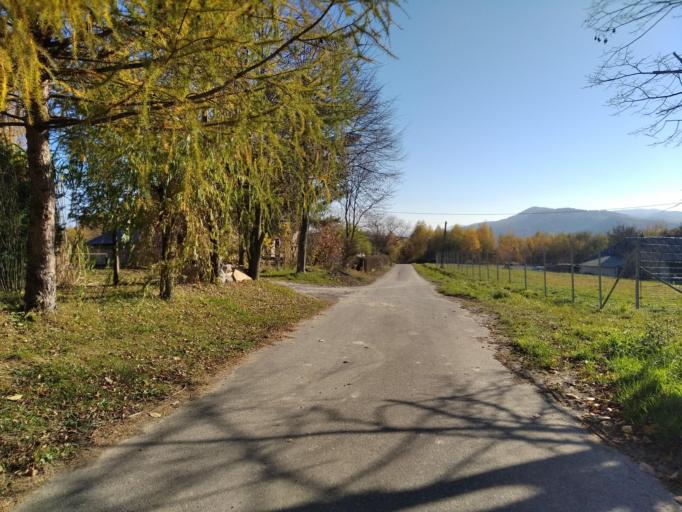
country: PL
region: Subcarpathian Voivodeship
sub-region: Powiat strzyzowski
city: Frysztak
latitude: 49.8622
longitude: 21.6055
